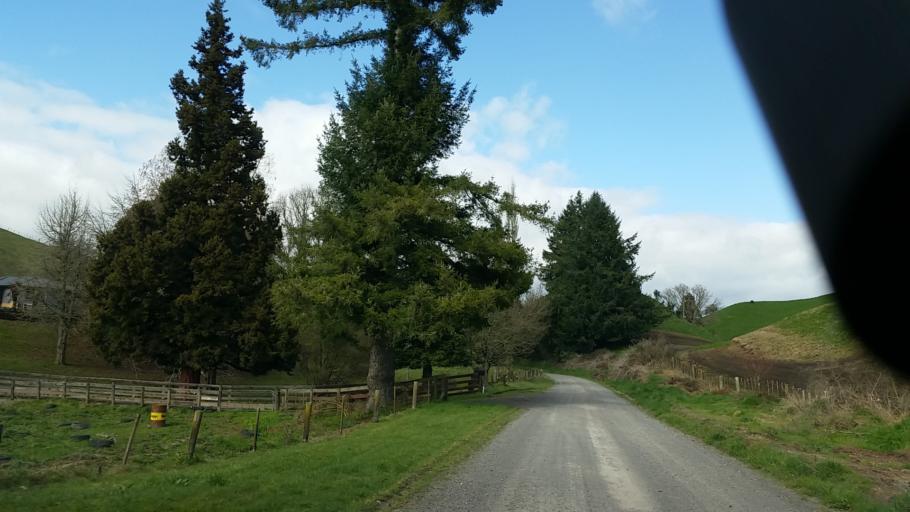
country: NZ
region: Waikato
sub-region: South Waikato District
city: Tokoroa
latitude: -38.3651
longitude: 176.0891
